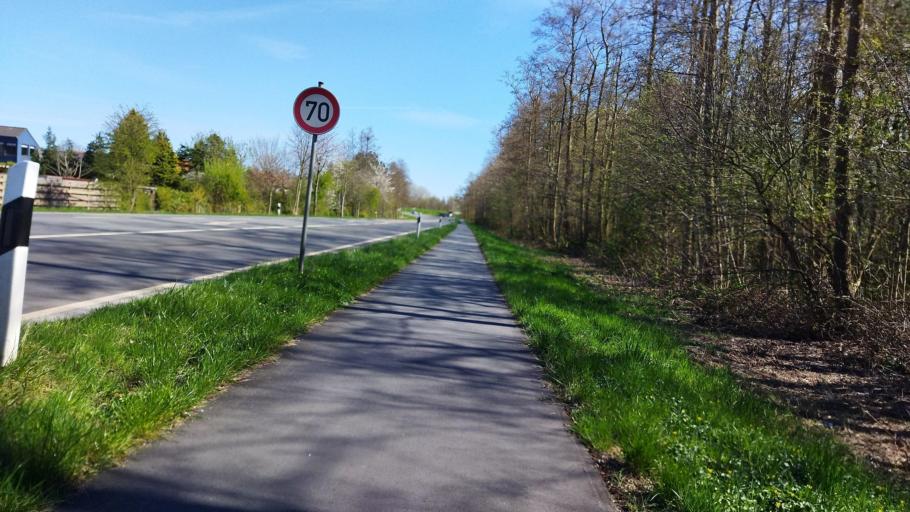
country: DE
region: Bremen
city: Bremerhaven
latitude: 53.5227
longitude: 8.5348
